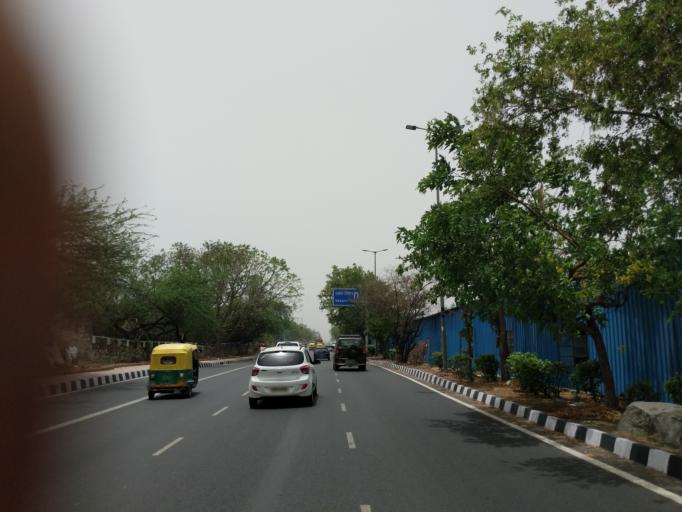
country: IN
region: NCT
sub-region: Central Delhi
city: Karol Bagh
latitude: 28.5462
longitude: 77.1610
